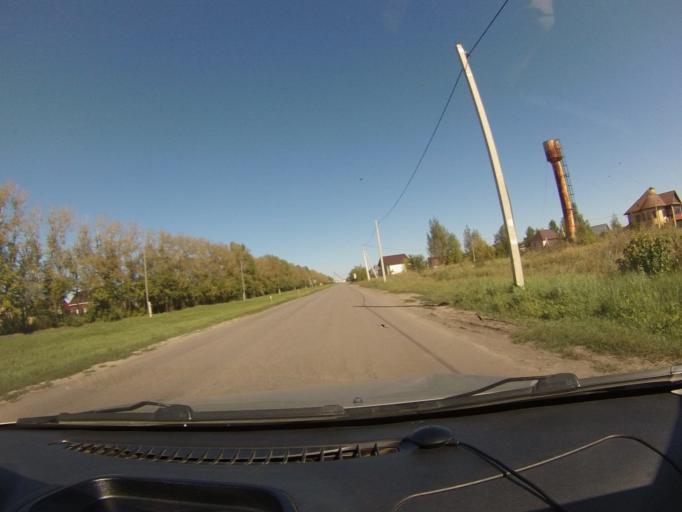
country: RU
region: Tambov
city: Komsomolets
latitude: 52.7697
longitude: 41.3660
